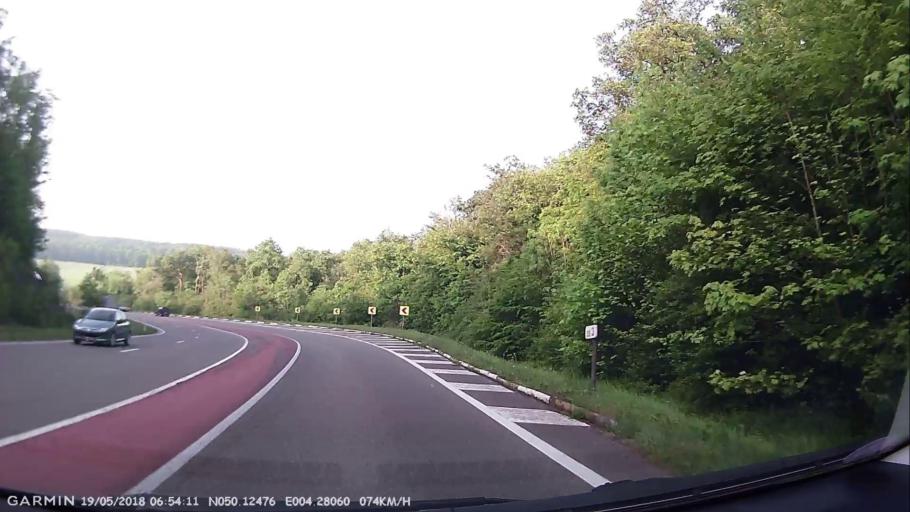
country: BE
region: Wallonia
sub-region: Province du Hainaut
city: Froidchapelle
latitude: 50.1247
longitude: 4.2805
